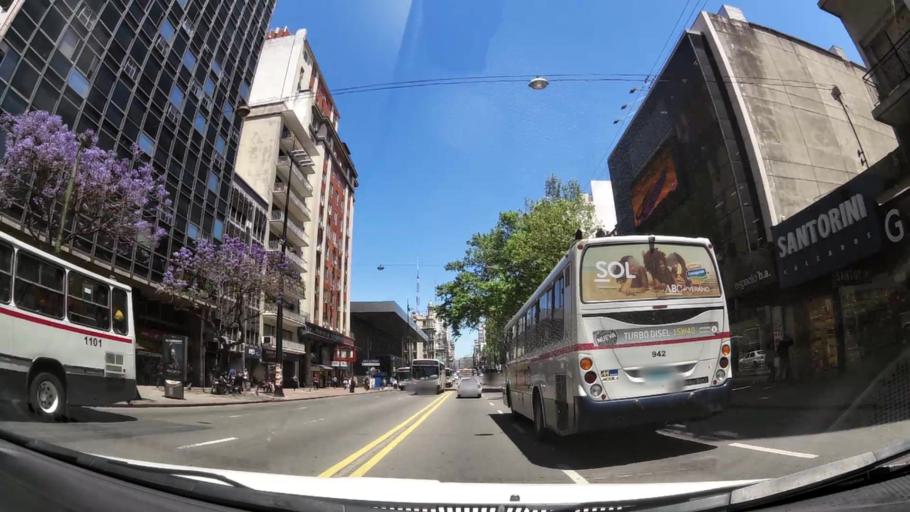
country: UY
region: Montevideo
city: Montevideo
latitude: -34.9030
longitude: -56.1788
